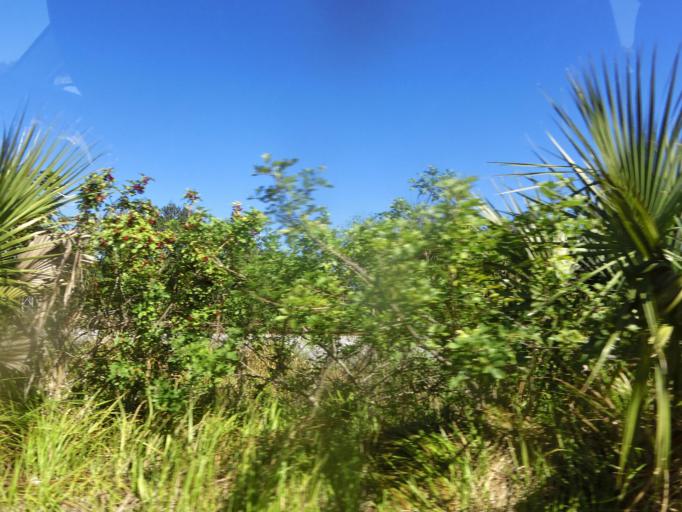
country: US
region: Florida
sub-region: Seminole County
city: Sanford
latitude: 28.8167
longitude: -81.3041
